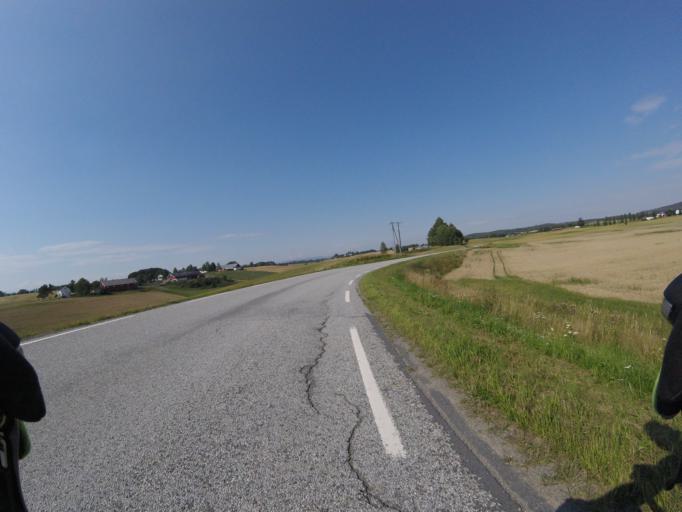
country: NO
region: Akershus
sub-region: Ullensaker
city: Klofta
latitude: 60.0910
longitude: 11.1606
